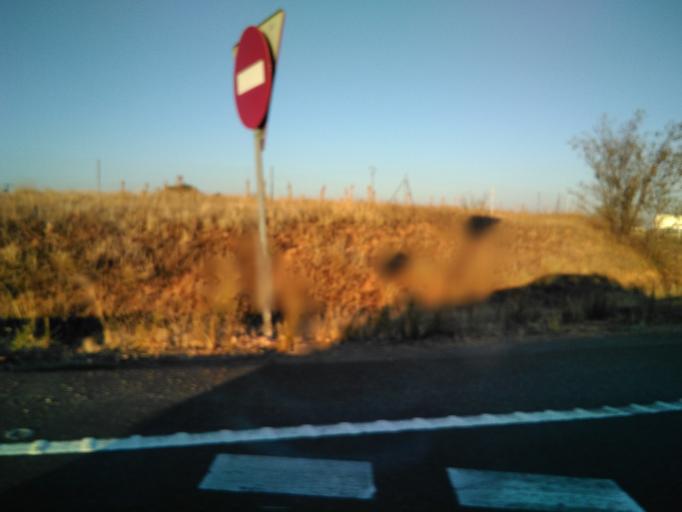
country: ES
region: Castille-La Mancha
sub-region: Provincia de Ciudad Real
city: Miguelturra
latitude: 38.9467
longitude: -3.9157
